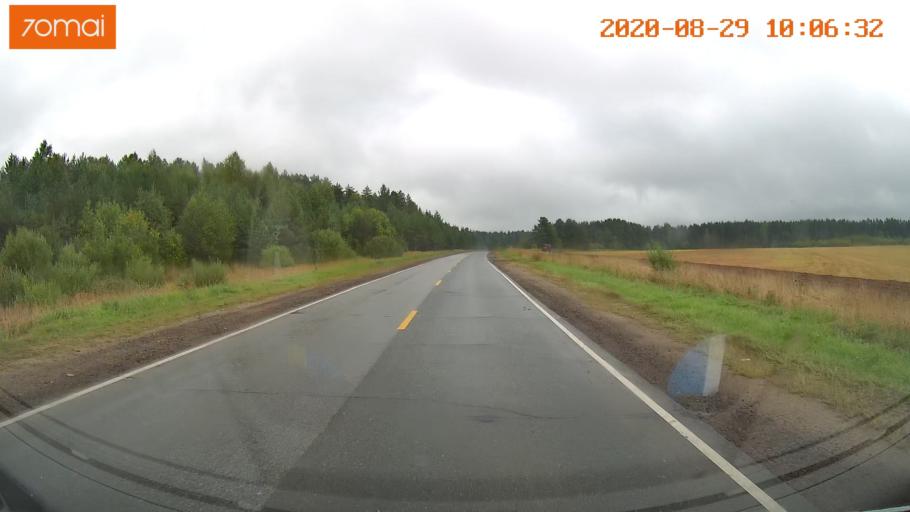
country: RU
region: Ivanovo
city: Kuznechikha
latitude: 57.3881
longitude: 42.5475
